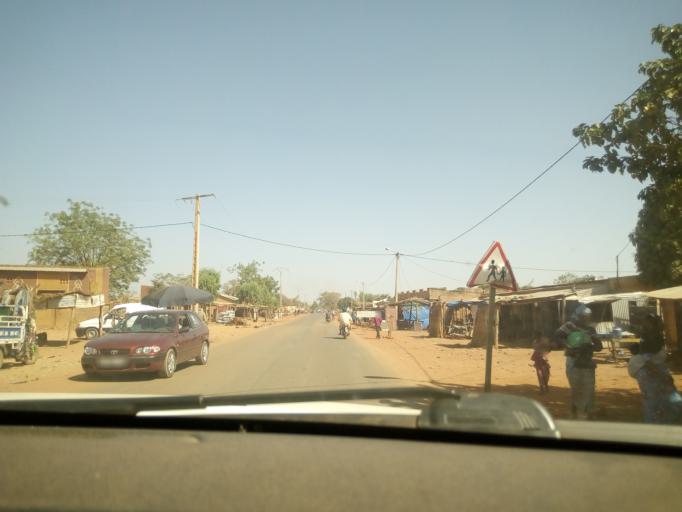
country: ML
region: Bamako
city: Bamako
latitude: 12.5873
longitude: -7.7664
